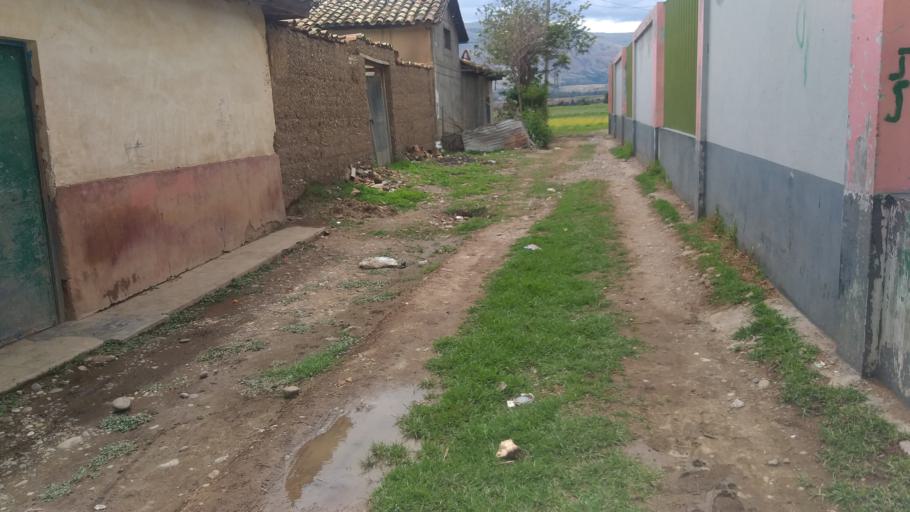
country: PE
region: Junin
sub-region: Provincia de Huancayo
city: Huayucachi
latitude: -12.1220
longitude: -75.2253
